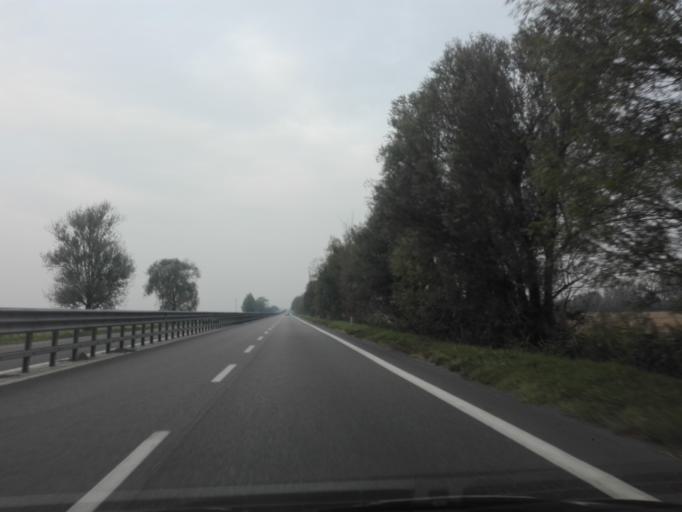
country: IT
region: Veneto
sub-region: Provincia di Rovigo
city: Pincara
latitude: 45.0237
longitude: 11.6169
